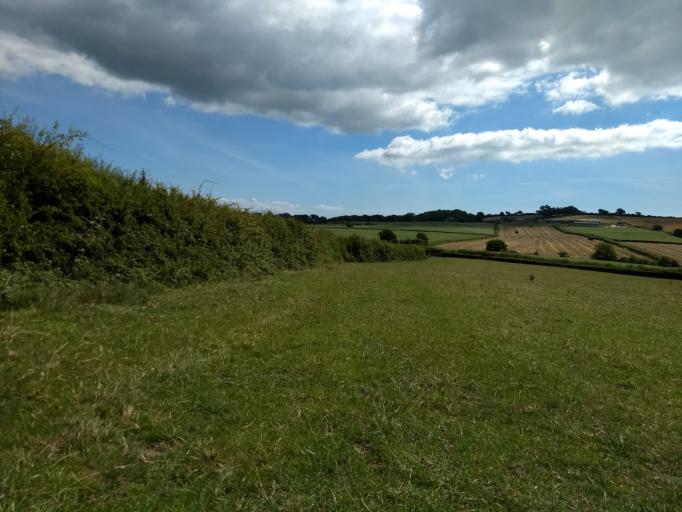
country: GB
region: England
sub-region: Isle of Wight
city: Ryde
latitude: 50.7103
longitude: -1.2007
